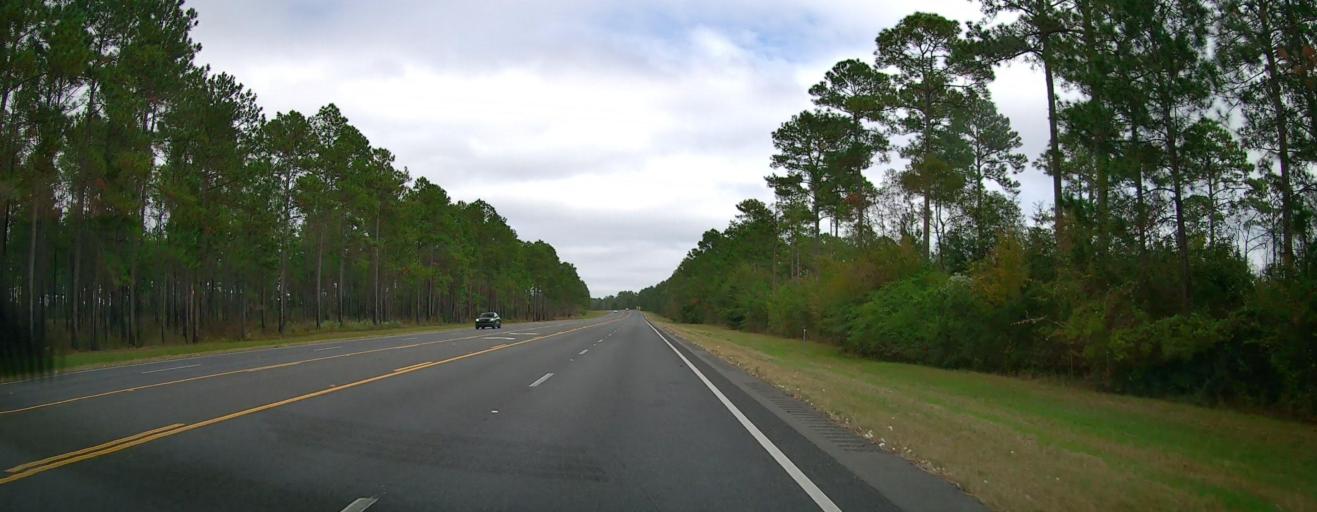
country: US
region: Georgia
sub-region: Colquitt County
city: Moultrie
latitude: 31.0410
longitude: -83.8476
